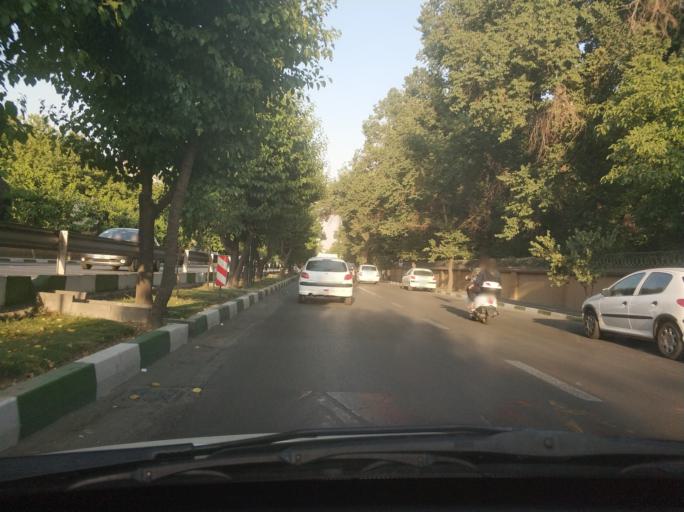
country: IR
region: Tehran
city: Tajrish
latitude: 35.8006
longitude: 51.4652
